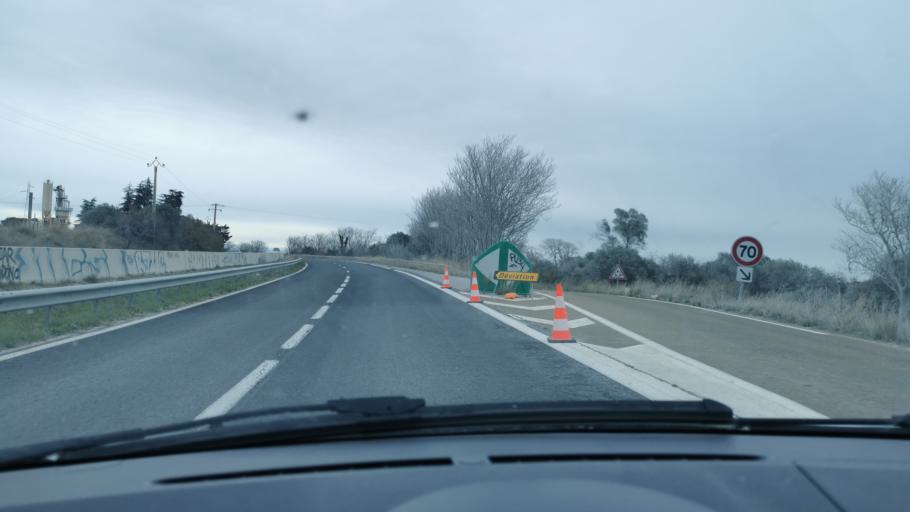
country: FR
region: Languedoc-Roussillon
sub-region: Departement de l'Herault
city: Mireval
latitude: 43.5272
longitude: 3.8209
